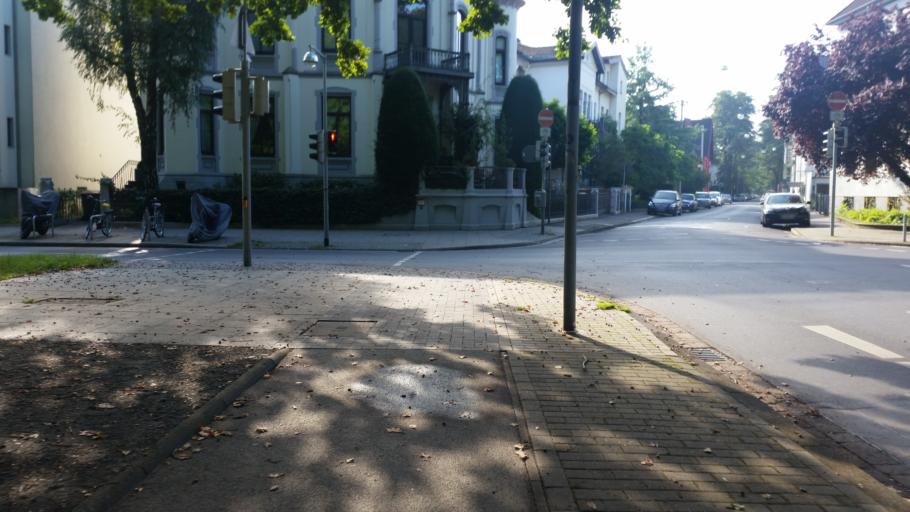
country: DE
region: Lower Saxony
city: Hannover
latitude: 52.3777
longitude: 9.7560
